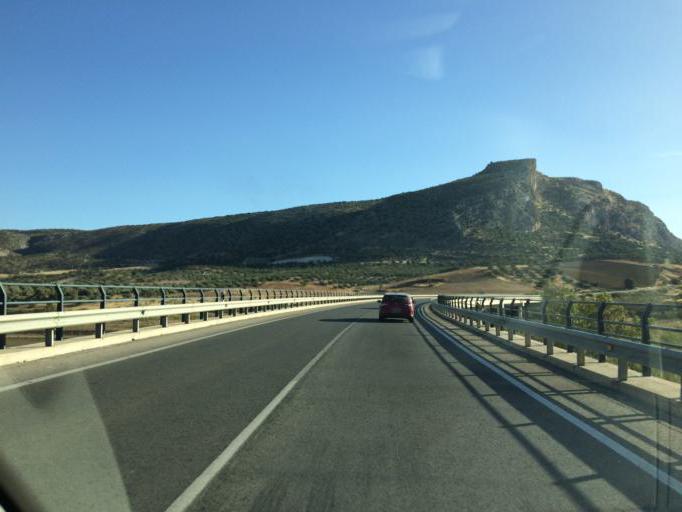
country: ES
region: Andalusia
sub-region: Provincia de Malaga
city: Teba
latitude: 36.9592
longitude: -4.8582
